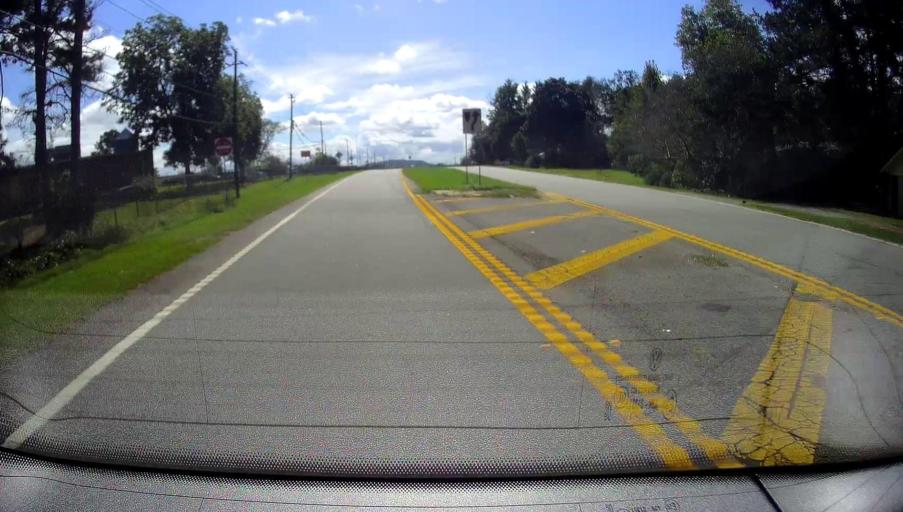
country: US
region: Georgia
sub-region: Bibb County
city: Macon
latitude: 32.8144
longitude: -83.5689
